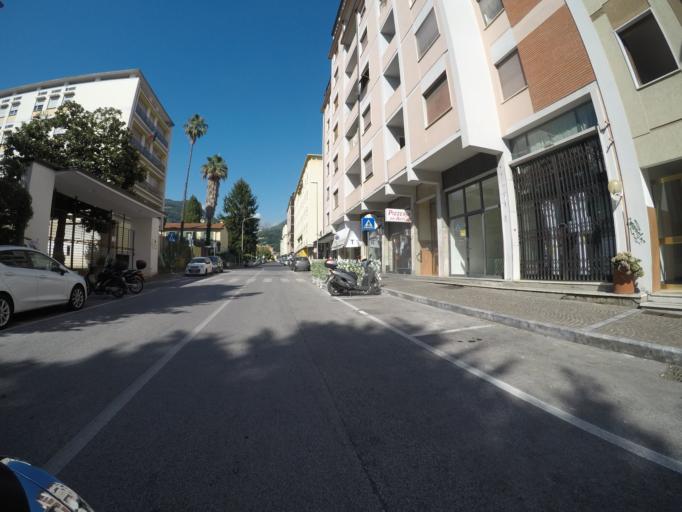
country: IT
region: Tuscany
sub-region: Provincia di Massa-Carrara
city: Massa
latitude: 44.0355
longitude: 10.1362
